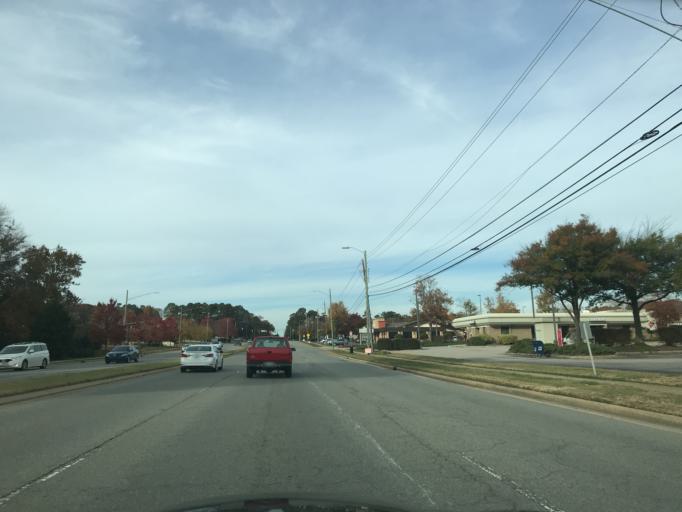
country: US
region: North Carolina
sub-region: Wake County
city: West Raleigh
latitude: 35.8866
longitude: -78.6795
